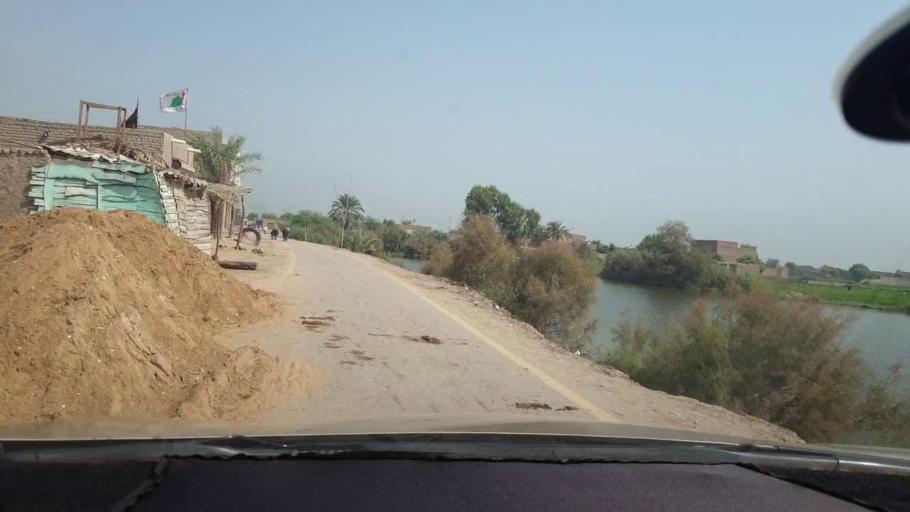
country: PK
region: Sindh
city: Kambar
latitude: 27.5793
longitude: 68.0066
